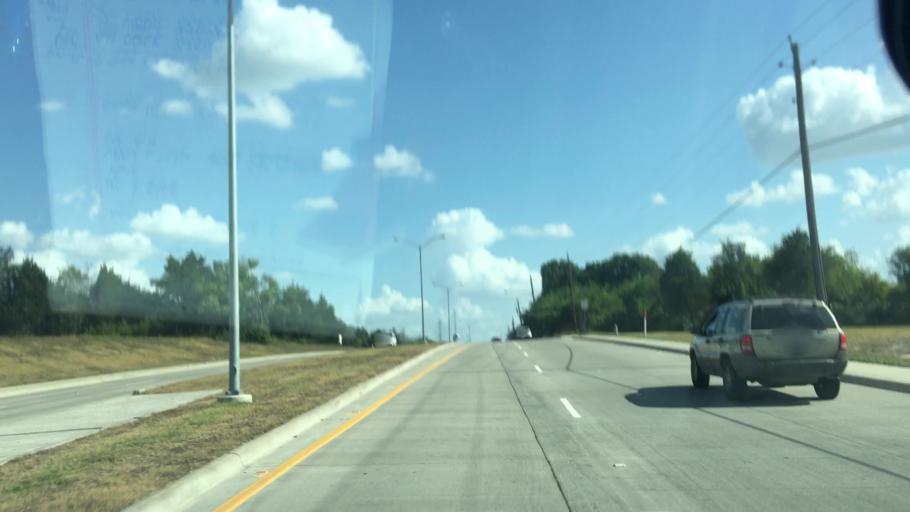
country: US
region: Texas
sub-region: Dallas County
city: Hutchins
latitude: 32.6446
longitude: -96.7514
